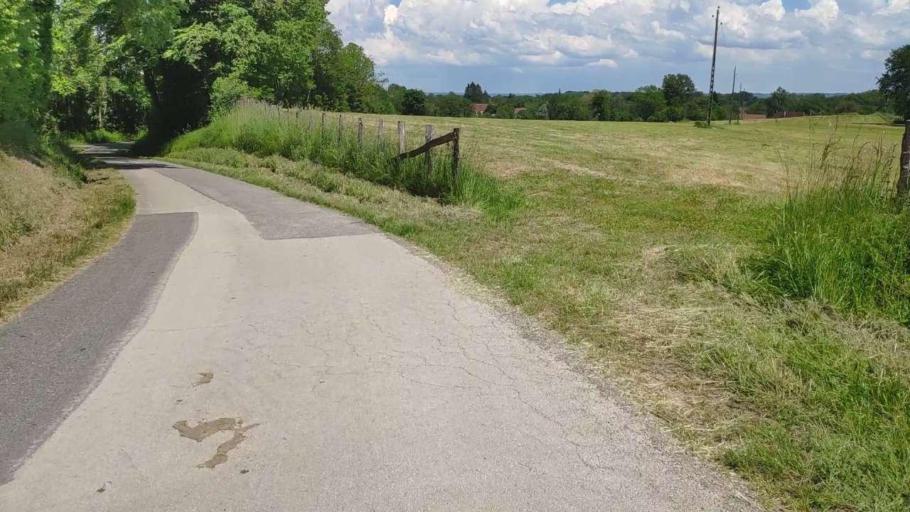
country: FR
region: Franche-Comte
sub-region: Departement du Jura
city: Bletterans
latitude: 46.7472
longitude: 5.3957
